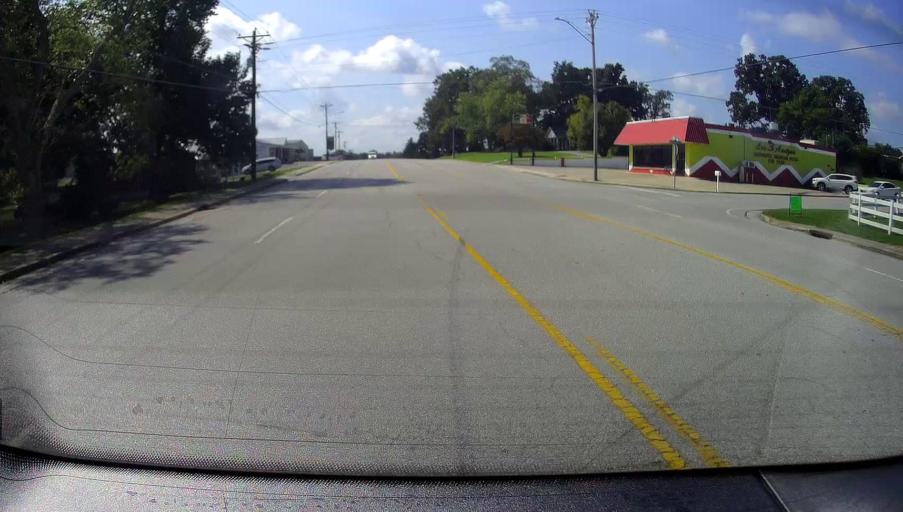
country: US
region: Tennessee
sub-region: Coffee County
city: Manchester
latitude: 35.4941
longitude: -86.0877
